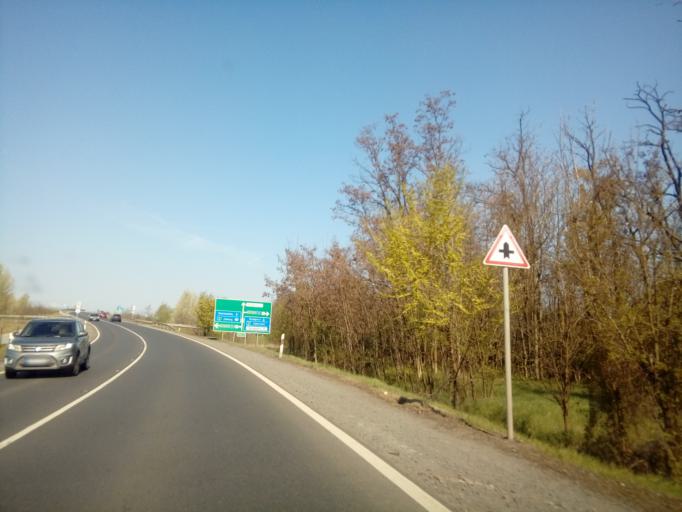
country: HU
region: Szabolcs-Szatmar-Bereg
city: Nagykallo
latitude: 47.8906
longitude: 21.8092
